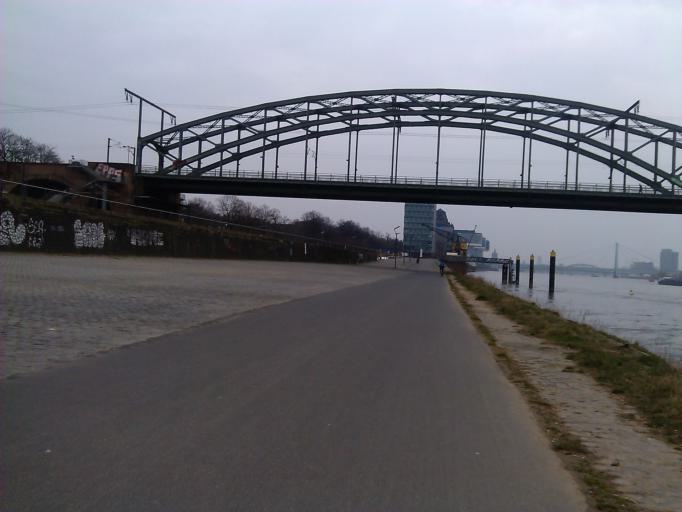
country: DE
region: North Rhine-Westphalia
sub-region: Regierungsbezirk Koln
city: Bayenthal
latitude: 50.9157
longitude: 6.9718
